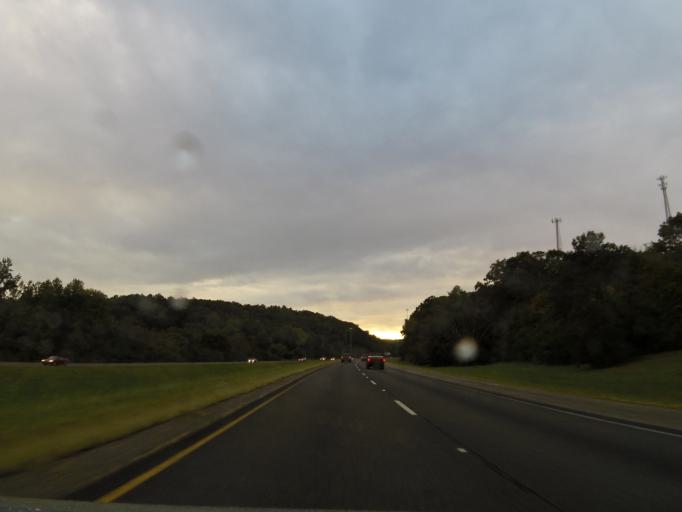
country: US
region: Alabama
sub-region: Jefferson County
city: Argo
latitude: 33.6634
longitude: -86.5643
